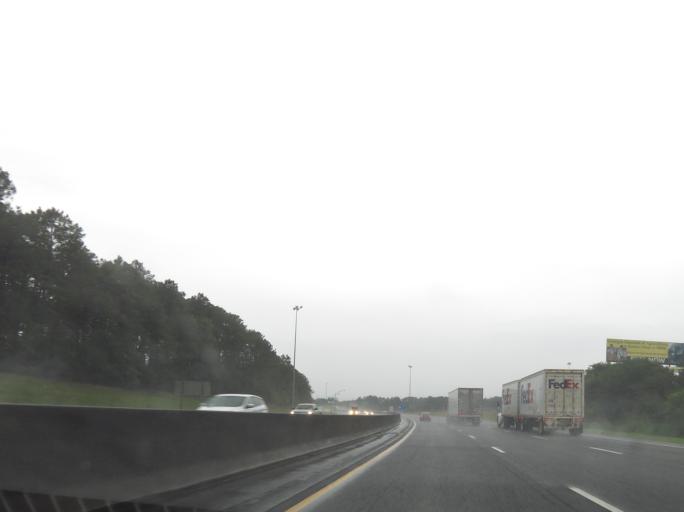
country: US
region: Georgia
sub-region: Tift County
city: Tifton
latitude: 31.4703
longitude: -83.5278
